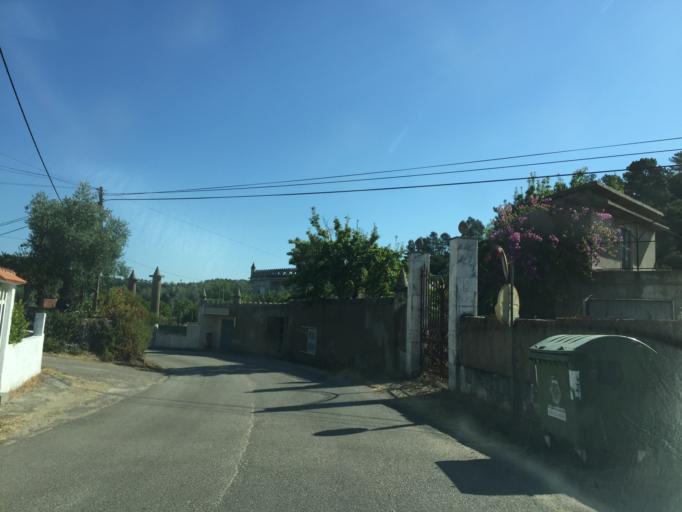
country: PT
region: Santarem
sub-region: Tomar
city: Tomar
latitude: 39.6021
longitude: -8.3269
